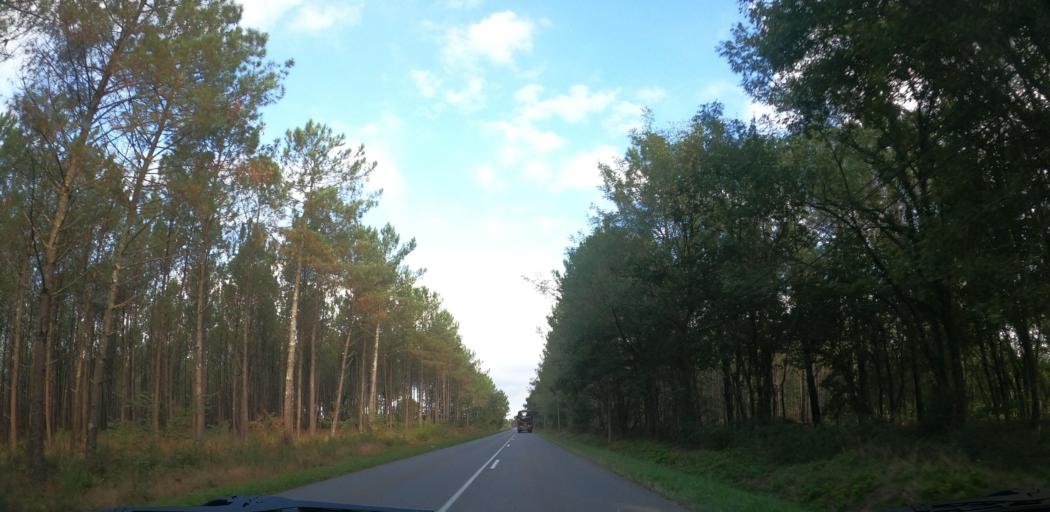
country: FR
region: Aquitaine
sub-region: Departement des Landes
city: Soustons
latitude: 43.7380
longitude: -1.2958
